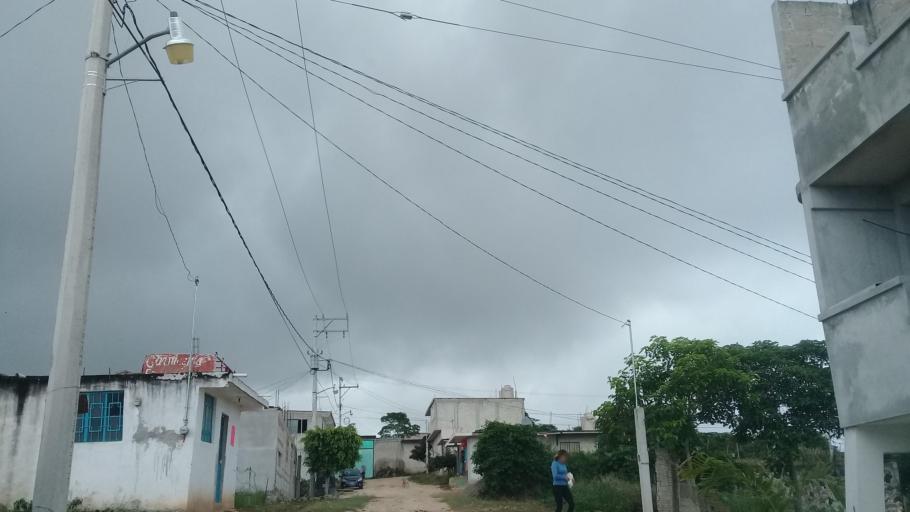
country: MX
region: Veracruz
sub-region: Emiliano Zapata
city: Jacarandas
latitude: 19.4910
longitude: -96.8537
